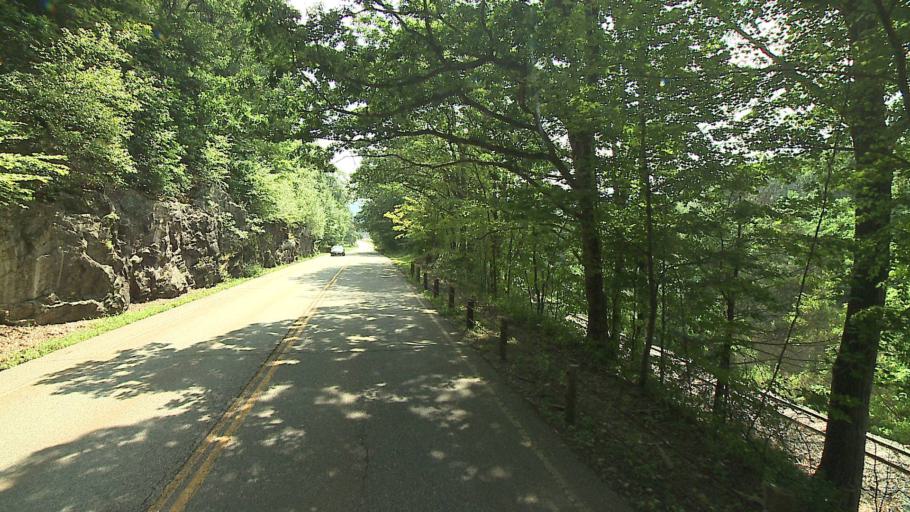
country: US
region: Connecticut
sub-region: Litchfield County
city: Thomaston
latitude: 41.6497
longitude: -73.0769
